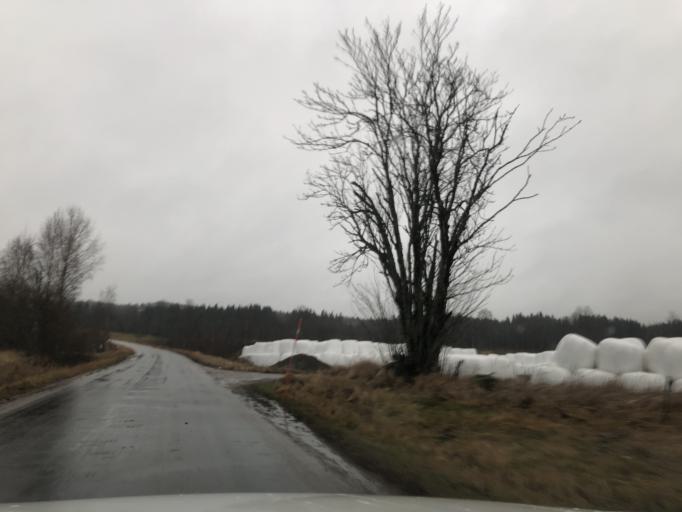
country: SE
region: Vaestra Goetaland
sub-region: Ulricehamns Kommun
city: Ulricehamn
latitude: 57.8584
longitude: 13.5514
